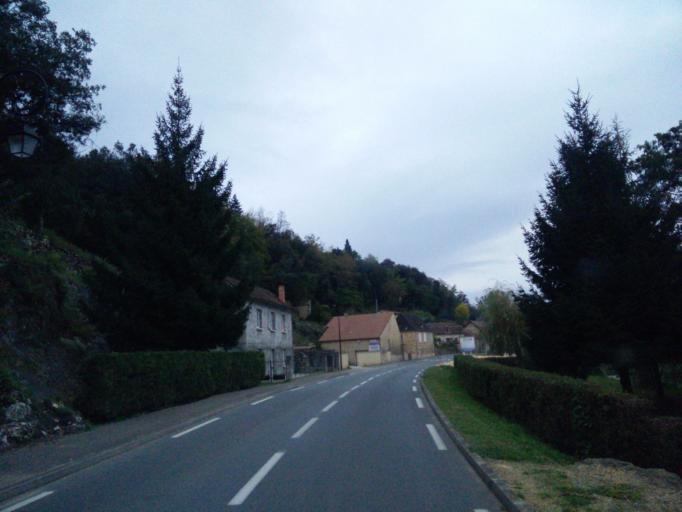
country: FR
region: Aquitaine
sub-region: Departement de la Dordogne
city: Carsac-Aillac
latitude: 44.8087
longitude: 1.2976
